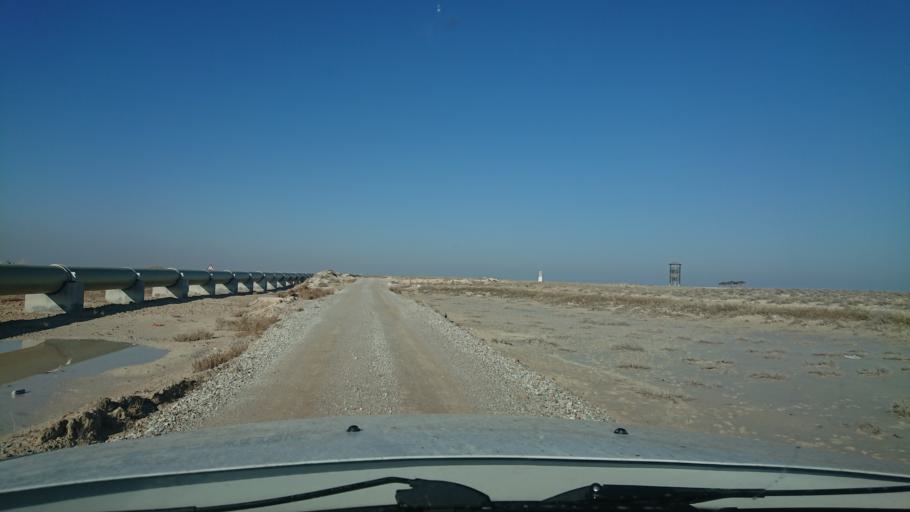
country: TR
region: Aksaray
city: Eskil
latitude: 38.4225
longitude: 33.5011
